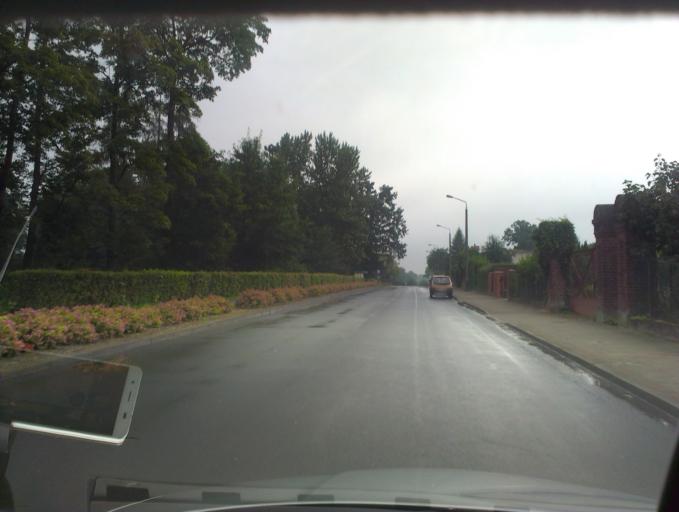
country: PL
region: West Pomeranian Voivodeship
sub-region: Powiat szczecinecki
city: Barwice
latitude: 53.7492
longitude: 16.3574
